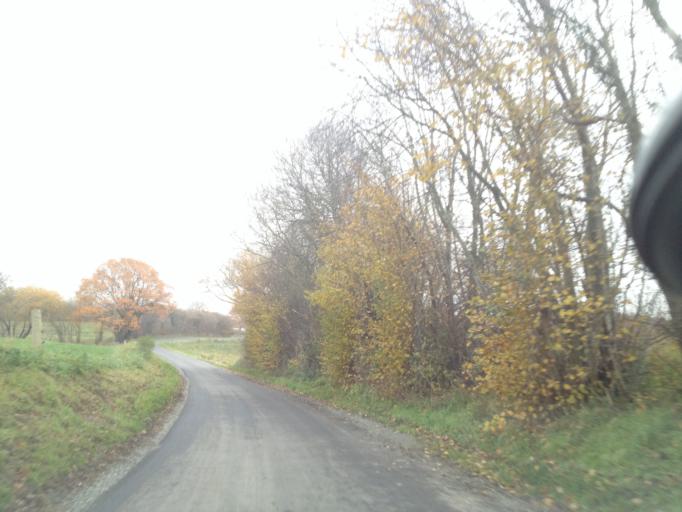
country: DK
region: South Denmark
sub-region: Nordfyns Kommune
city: Sonderso
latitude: 55.4258
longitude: 10.2240
